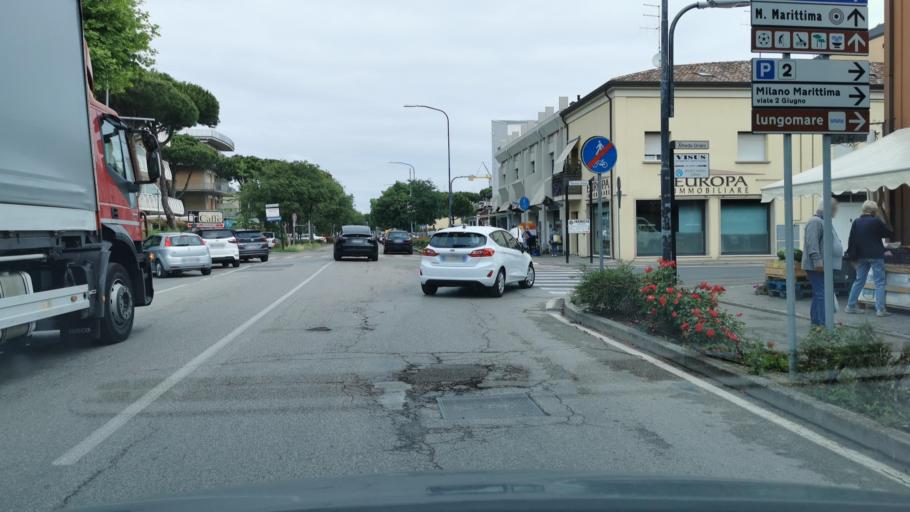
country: IT
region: Emilia-Romagna
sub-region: Provincia di Ravenna
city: Cervia
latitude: 44.2632
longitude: 12.3480
